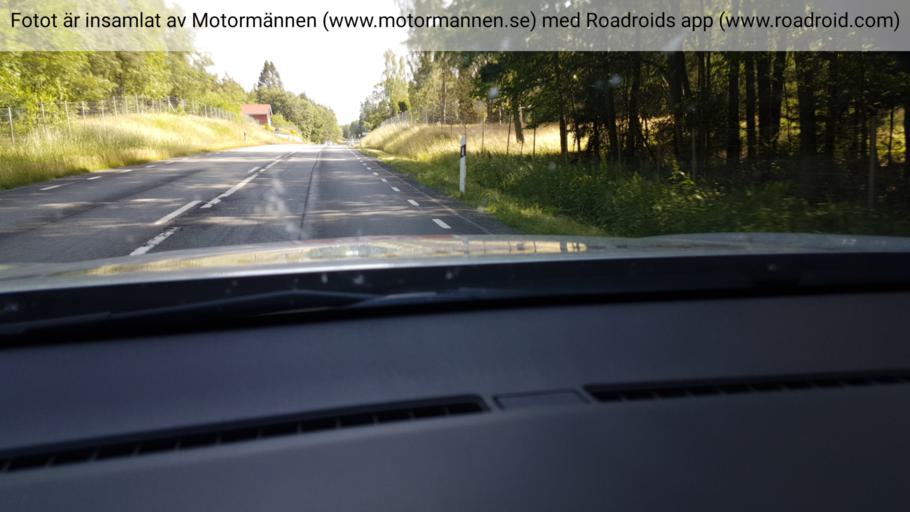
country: SE
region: Joenkoeping
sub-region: Eksjo Kommun
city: Eksjoe
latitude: 57.7330
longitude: 14.9367
